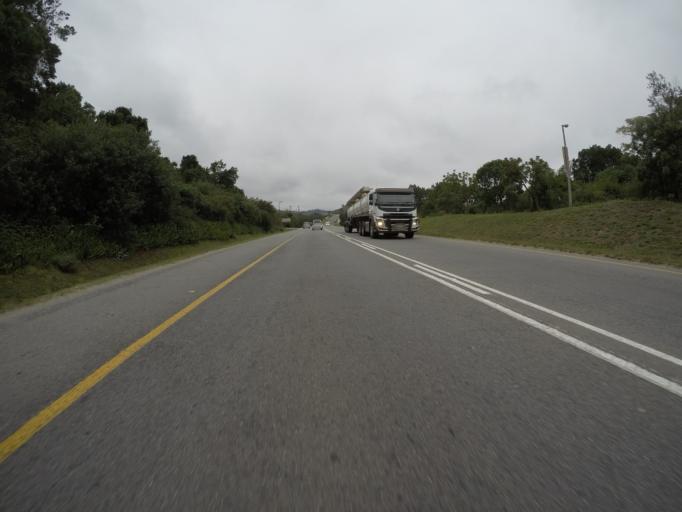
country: ZA
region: Western Cape
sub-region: Eden District Municipality
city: Knysna
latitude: -34.0412
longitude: 23.0761
